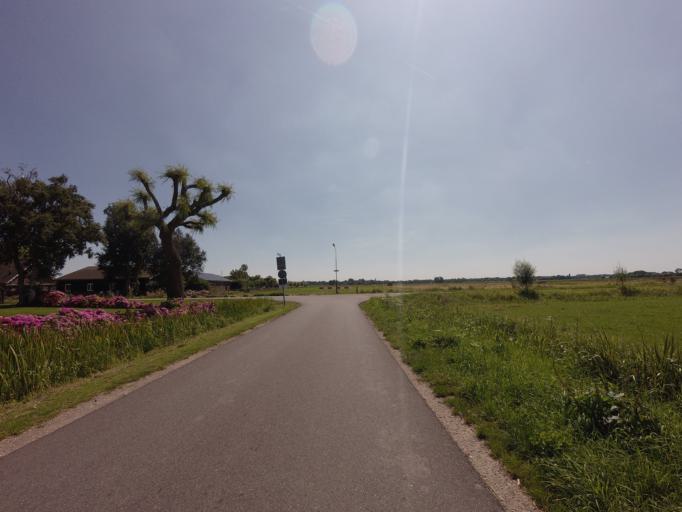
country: NL
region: Utrecht
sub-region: Stichtse Vecht
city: Maarssen
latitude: 52.1605
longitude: 5.0666
